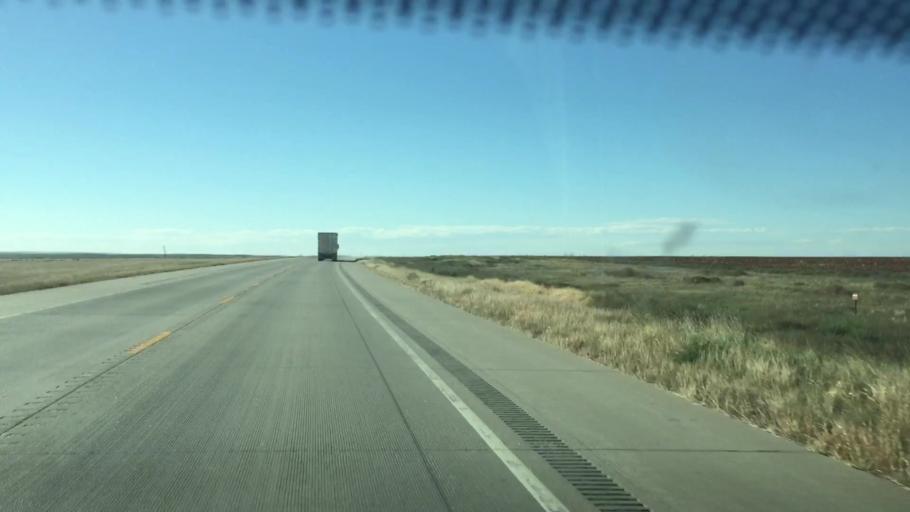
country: US
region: Colorado
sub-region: Kiowa County
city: Eads
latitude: 38.7884
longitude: -102.9283
